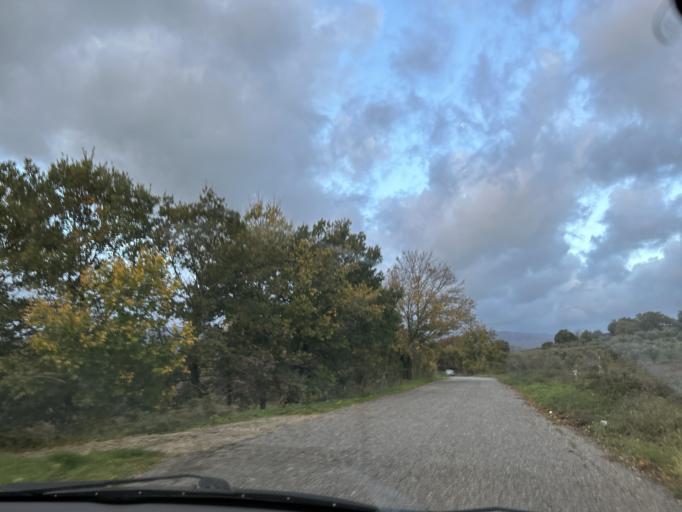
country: IT
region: Calabria
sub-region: Provincia di Catanzaro
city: Squillace
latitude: 38.7744
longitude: 16.5024
